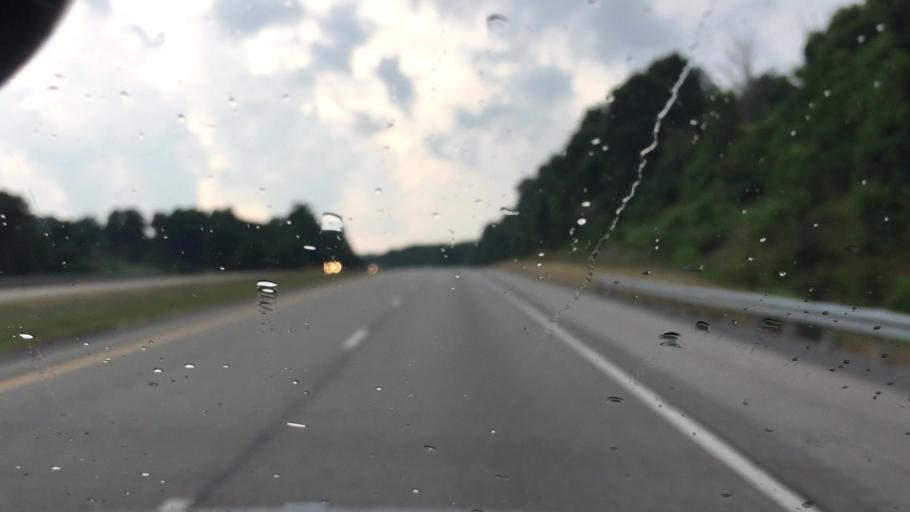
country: US
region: West Virginia
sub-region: Monongalia County
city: Cheat Lake
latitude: 39.6558
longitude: -79.6906
